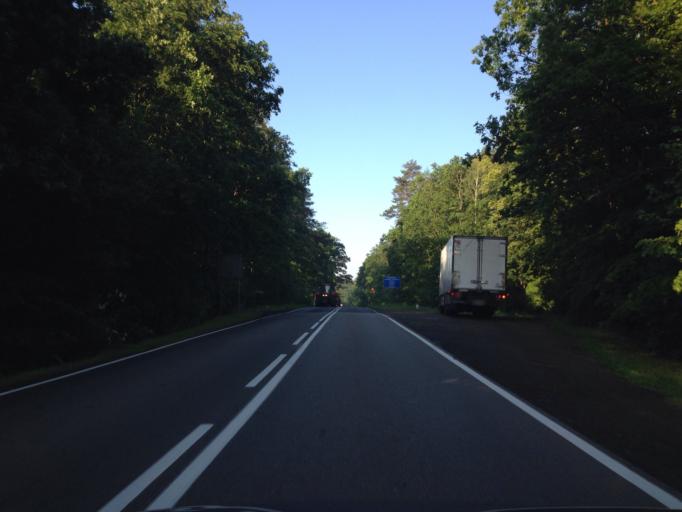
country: PL
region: Pomeranian Voivodeship
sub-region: Powiat kwidzynski
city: Gardeja
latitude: 53.5875
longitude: 18.9075
